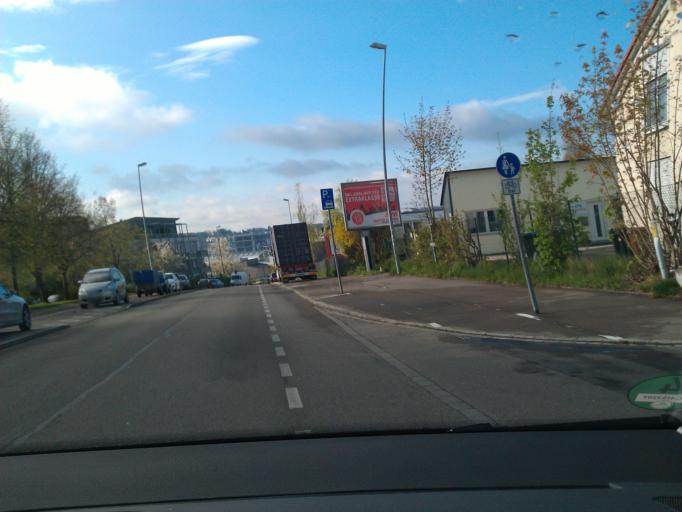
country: DE
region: Baden-Wuerttemberg
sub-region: Tuebingen Region
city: Ulm
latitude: 48.4056
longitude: 9.9569
